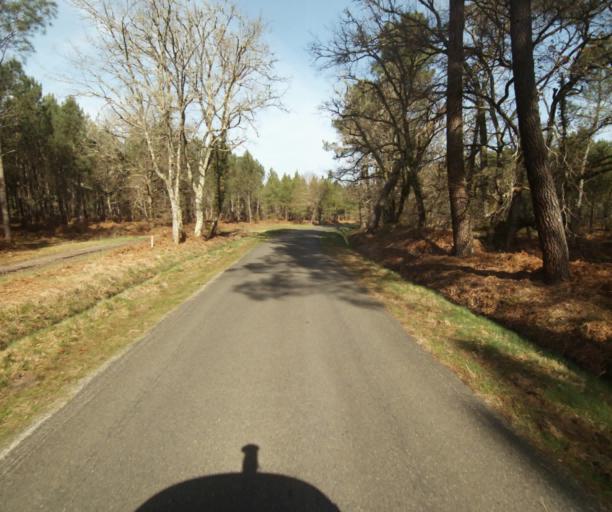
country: FR
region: Aquitaine
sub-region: Departement de la Gironde
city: Bazas
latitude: 44.2342
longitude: -0.2021
